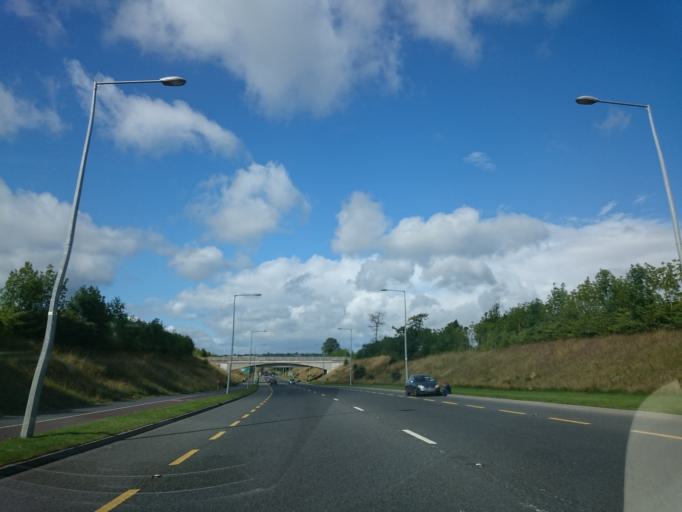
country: IE
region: Leinster
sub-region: Kilkenny
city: Kilkenny
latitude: 52.6769
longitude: -7.2463
